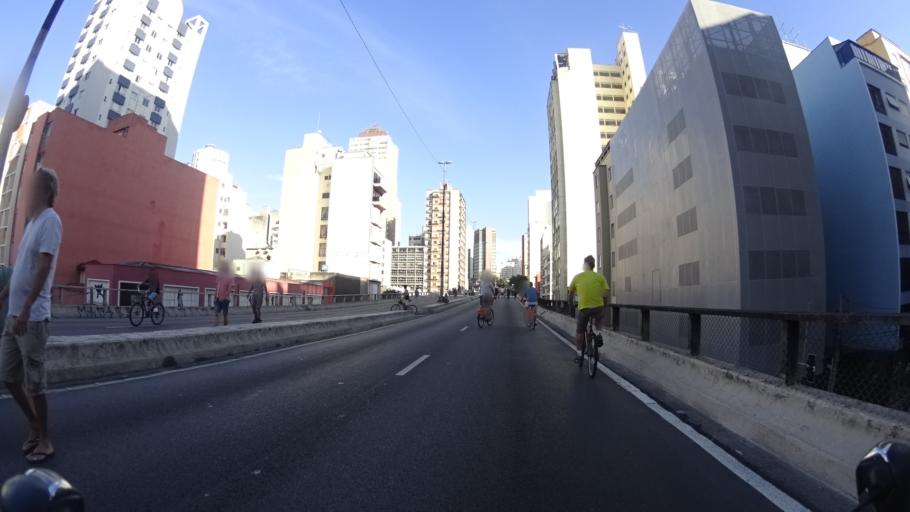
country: BR
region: Sao Paulo
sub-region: Sao Paulo
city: Sao Paulo
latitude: -23.5435
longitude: -46.6479
